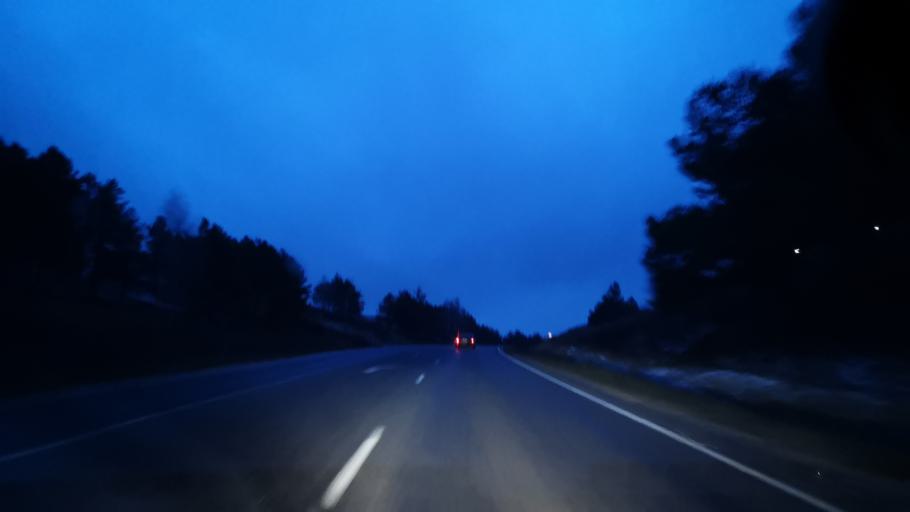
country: MD
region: Orhei
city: Orhei
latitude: 47.4003
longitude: 28.8065
